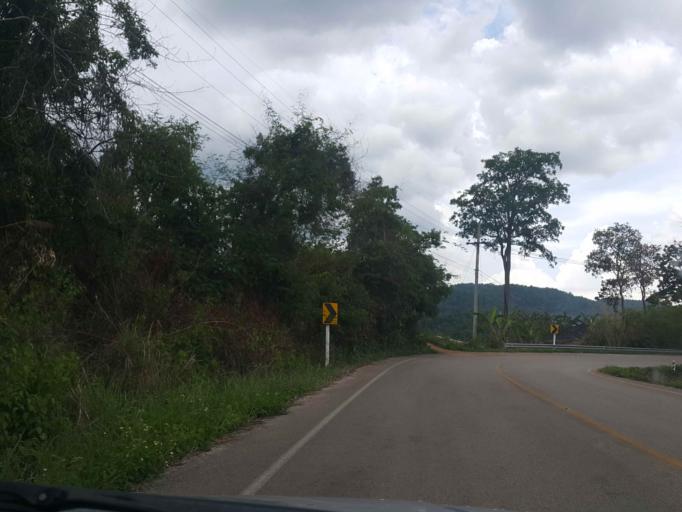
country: TH
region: Lampang
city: Ngao
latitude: 18.9340
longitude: 100.0886
